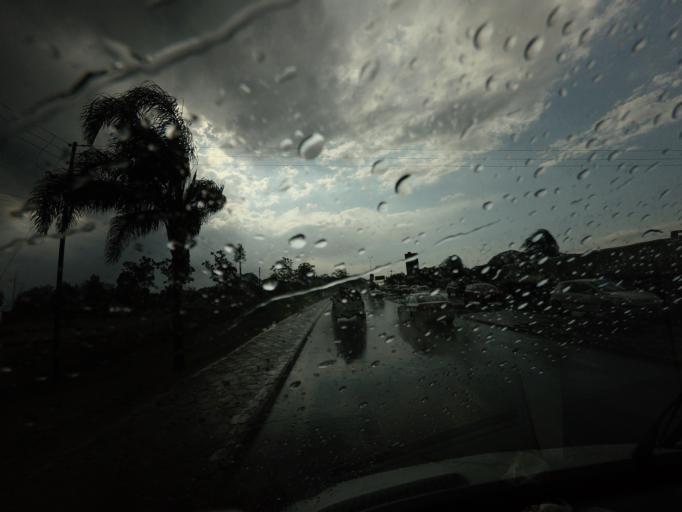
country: SZ
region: Manzini
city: Manzini
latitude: -26.4976
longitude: 31.3606
